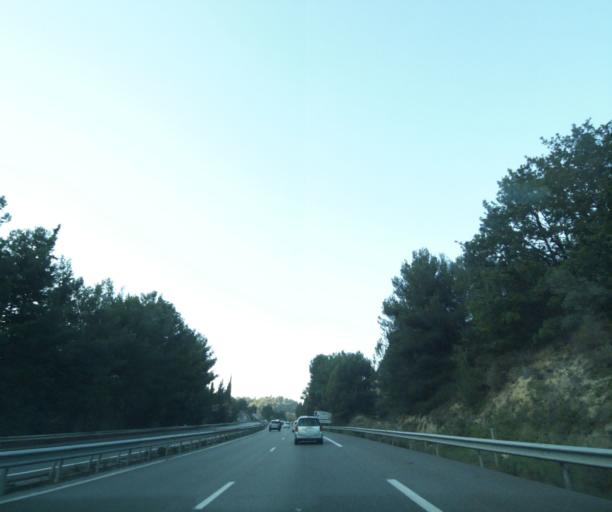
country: FR
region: Provence-Alpes-Cote d'Azur
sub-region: Departement des Bouches-du-Rhone
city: La Destrousse
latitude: 43.3664
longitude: 5.6124
